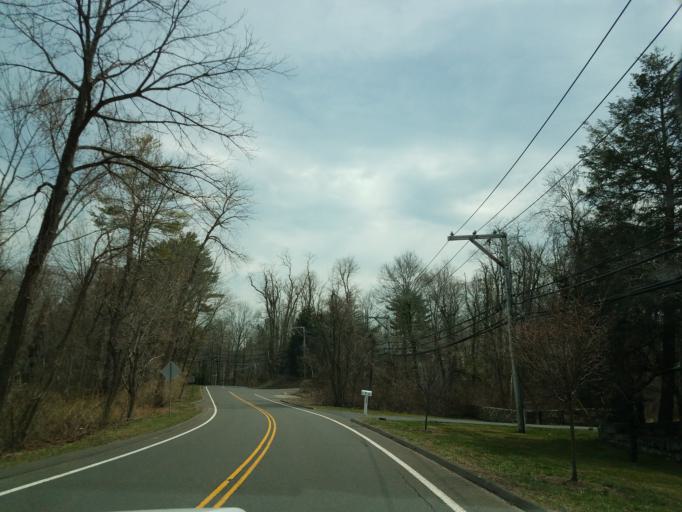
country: US
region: Connecticut
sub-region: Fairfield County
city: Glenville
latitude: 41.0776
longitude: -73.6419
